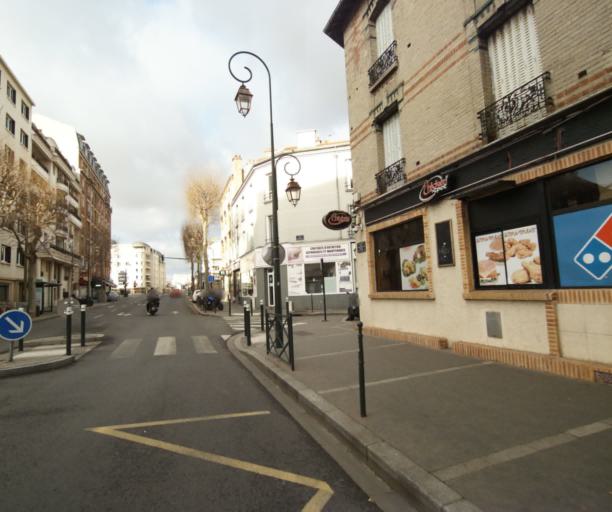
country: FR
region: Ile-de-France
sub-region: Departement des Hauts-de-Seine
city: Colombes
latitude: 48.9125
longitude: 2.2539
